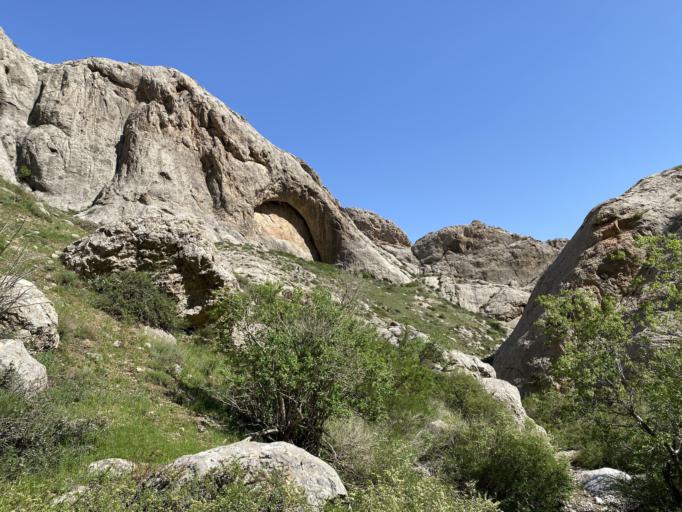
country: KZ
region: Ongtustik Qazaqstan
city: Ashchysay
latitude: 43.7732
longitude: 68.8099
